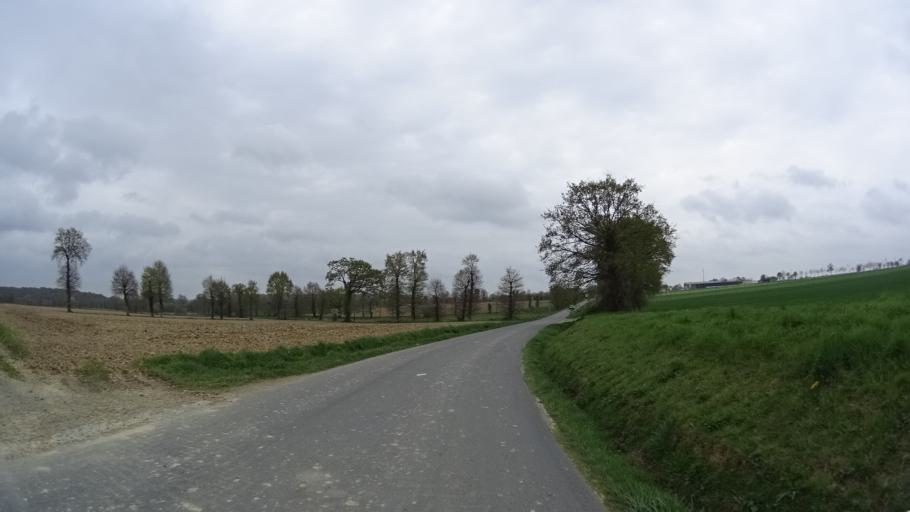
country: FR
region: Brittany
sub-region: Departement d'Ille-et-Vilaine
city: La Chapelle-Thouarault
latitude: 48.1160
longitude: -1.8713
